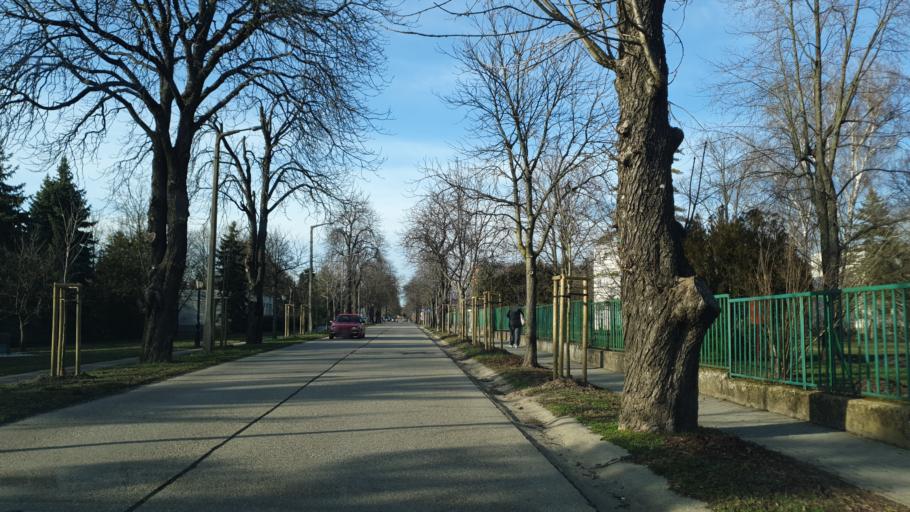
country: HU
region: Fejer
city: Etyek
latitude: 47.4986
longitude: 18.7530
